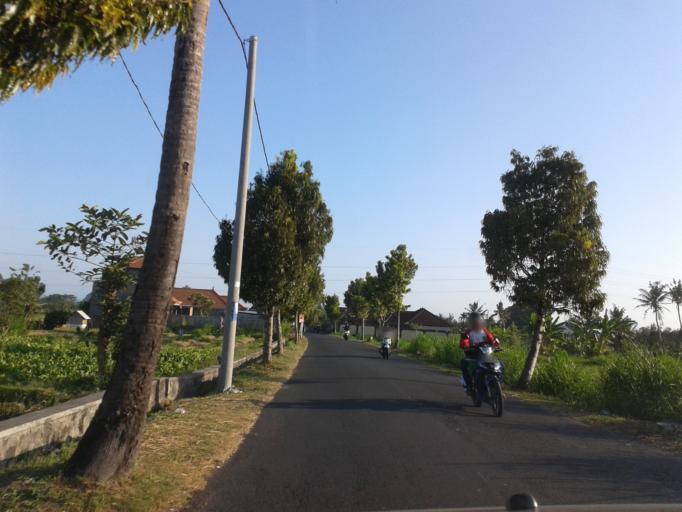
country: ID
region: Bali
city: Semarapura
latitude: -8.5609
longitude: 115.3866
